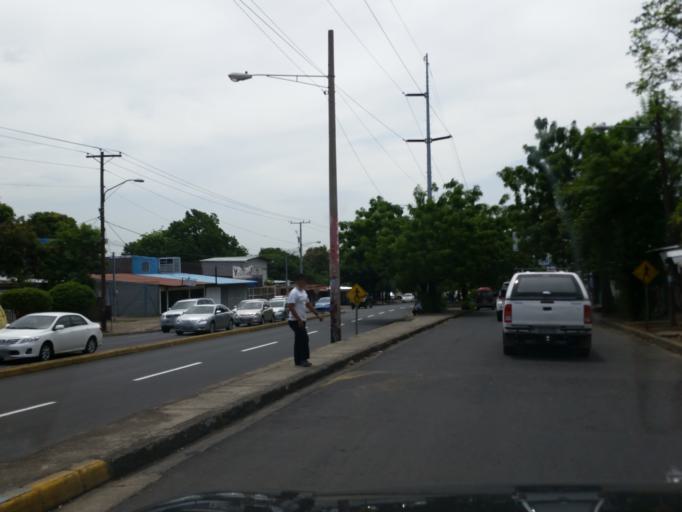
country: NI
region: Managua
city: Managua
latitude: 12.1204
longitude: -86.2736
